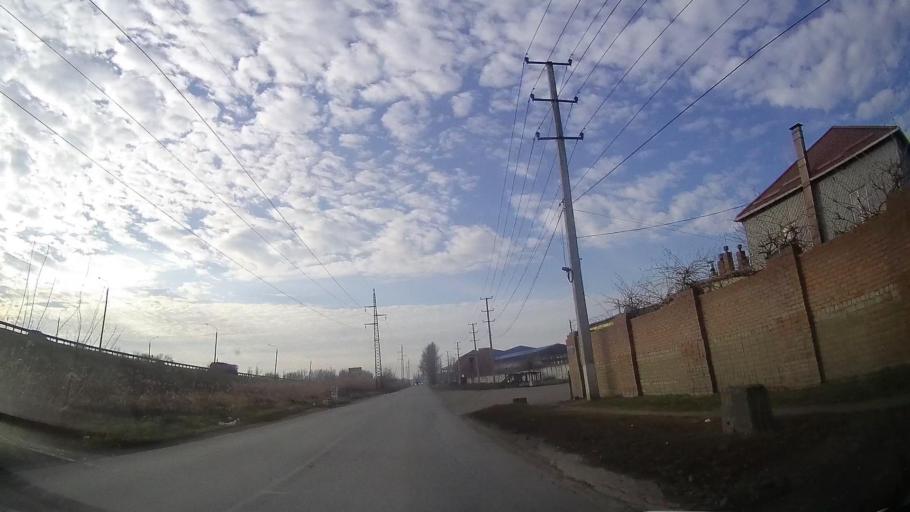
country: RU
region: Rostov
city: Bataysk
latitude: 47.1184
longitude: 39.7685
